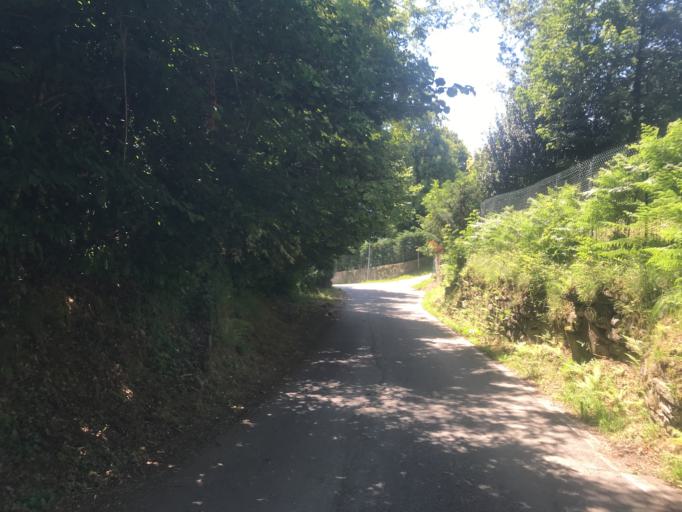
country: IT
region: Piedmont
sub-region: Provincia di Novara
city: Pisano
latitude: 45.8057
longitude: 8.5104
